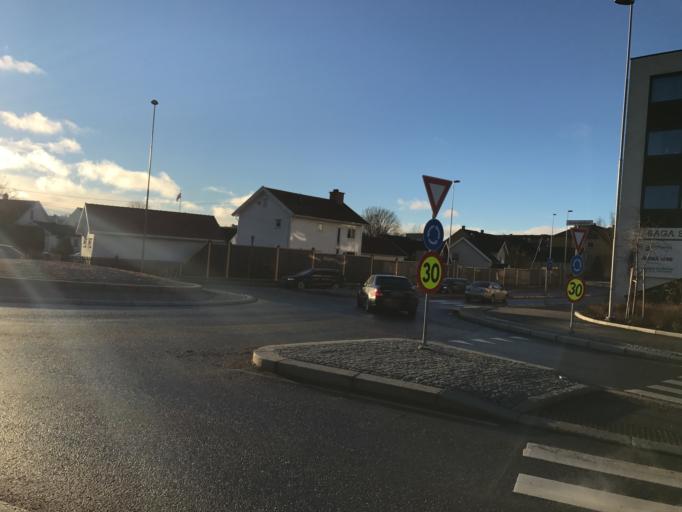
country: NO
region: Akershus
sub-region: Ullensaker
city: Jessheim
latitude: 60.1411
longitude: 11.1810
